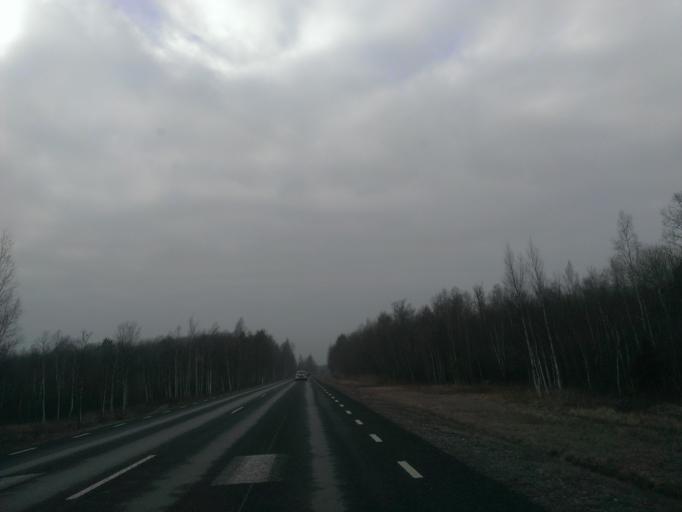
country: EE
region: Saare
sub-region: Orissaare vald
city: Orissaare
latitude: 58.5811
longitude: 23.3573
